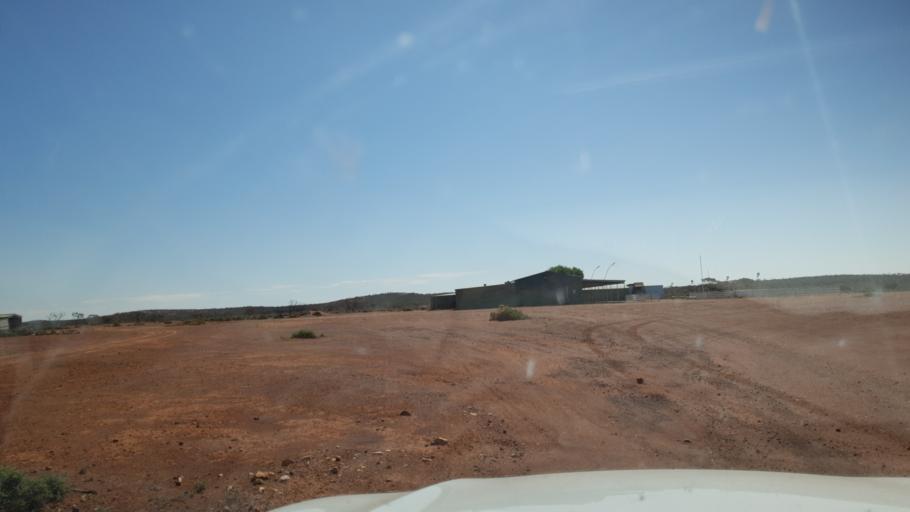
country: AU
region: South Australia
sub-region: Kimba
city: Caralue
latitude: -32.5083
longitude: 136.4904
